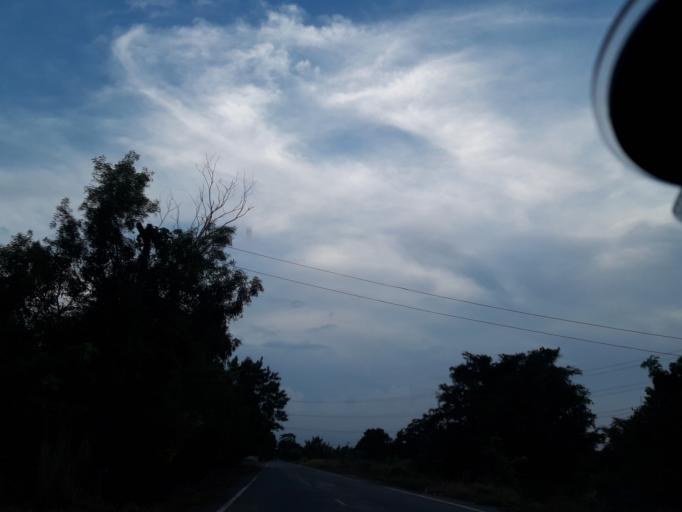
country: TH
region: Pathum Thani
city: Nong Suea
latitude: 14.1889
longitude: 100.8689
